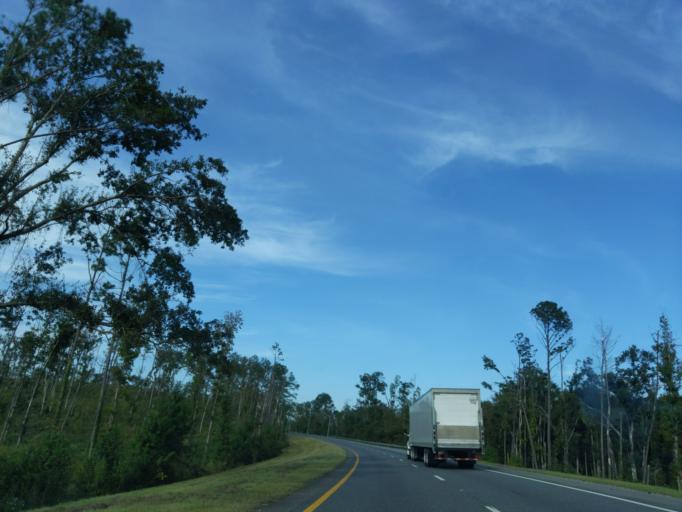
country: US
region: Florida
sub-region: Gadsden County
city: Chattahoochee
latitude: 30.6332
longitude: -84.8820
